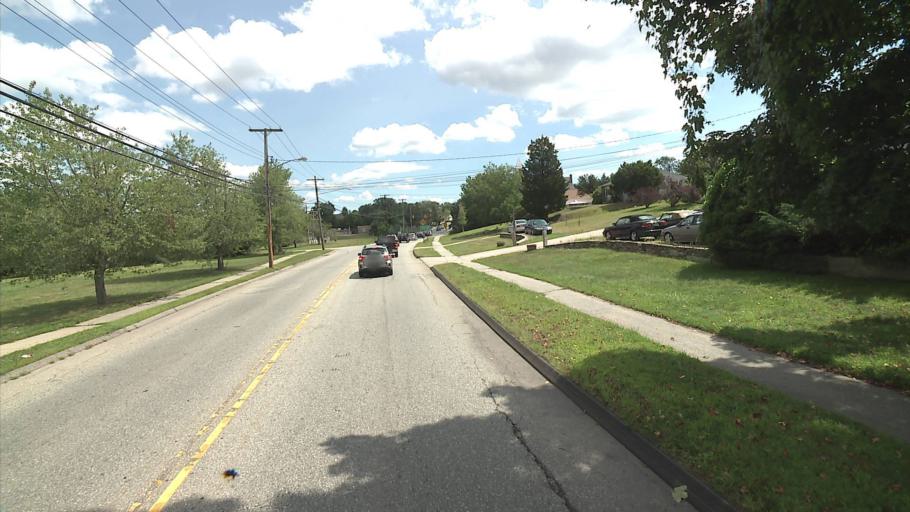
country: US
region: Connecticut
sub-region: New London County
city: Long Hill
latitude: 41.3469
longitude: -72.0409
